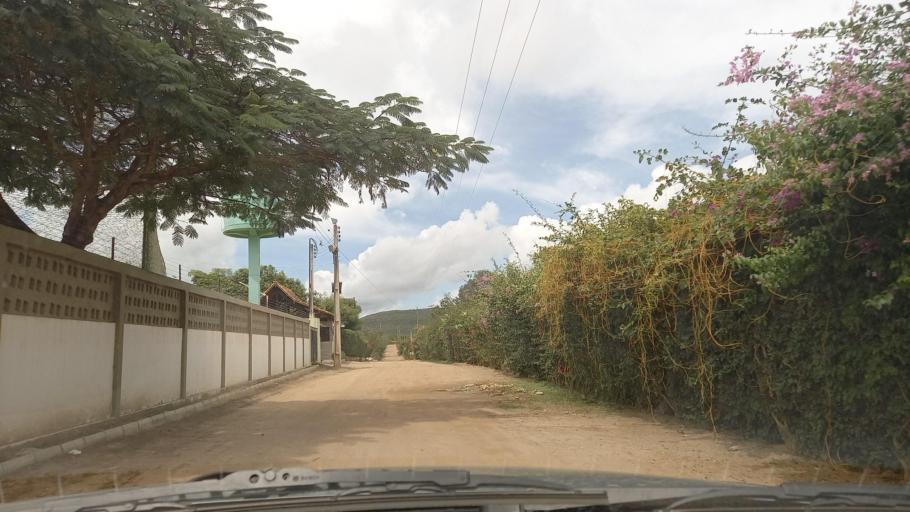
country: BR
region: Pernambuco
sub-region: Gravata
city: Gravata
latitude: -8.1969
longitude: -35.5892
